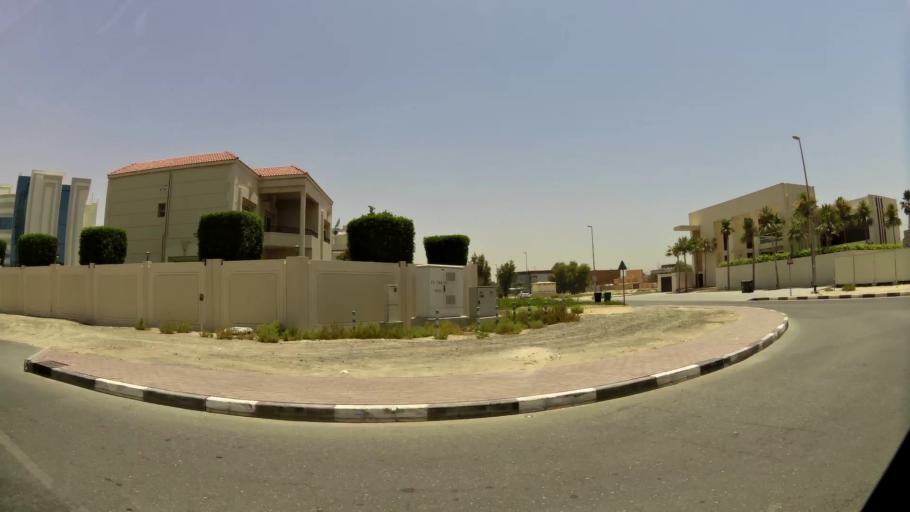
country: AE
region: Dubai
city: Dubai
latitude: 25.0920
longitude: 55.1986
